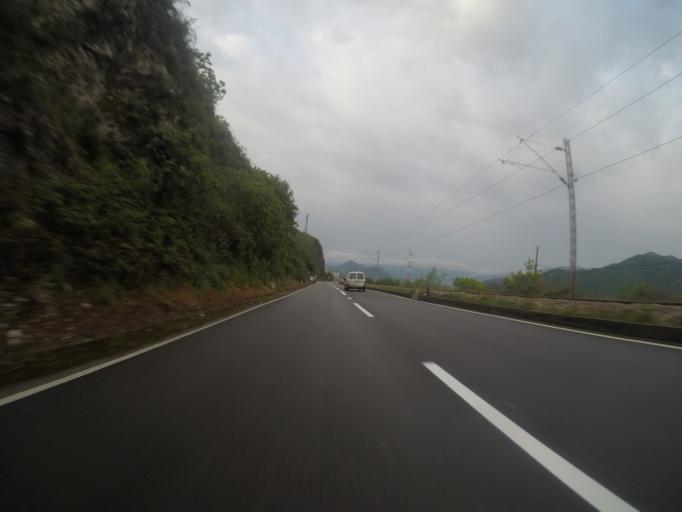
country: ME
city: Mojanovici
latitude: 42.2751
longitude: 19.1248
